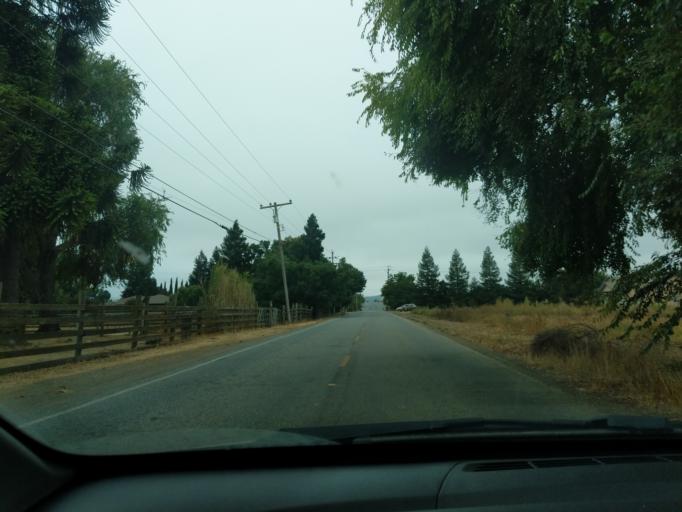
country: US
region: California
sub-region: Santa Clara County
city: Gilroy
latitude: 37.0454
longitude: -121.5716
